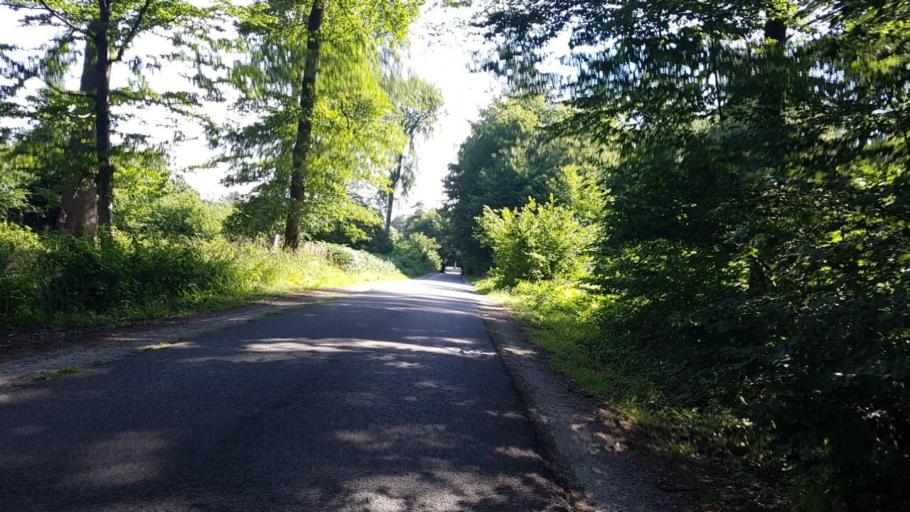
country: FR
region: Picardie
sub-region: Departement de l'Oise
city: Pontpoint
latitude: 49.2891
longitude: 2.6312
